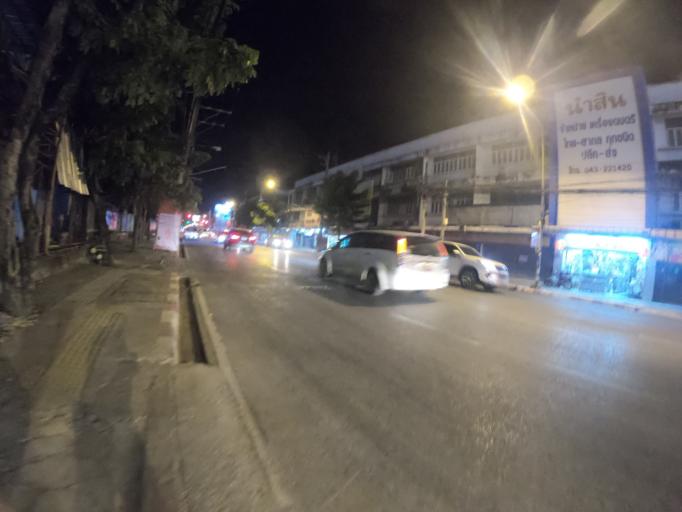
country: TH
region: Khon Kaen
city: Khon Kaen
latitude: 16.4307
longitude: 102.8343
